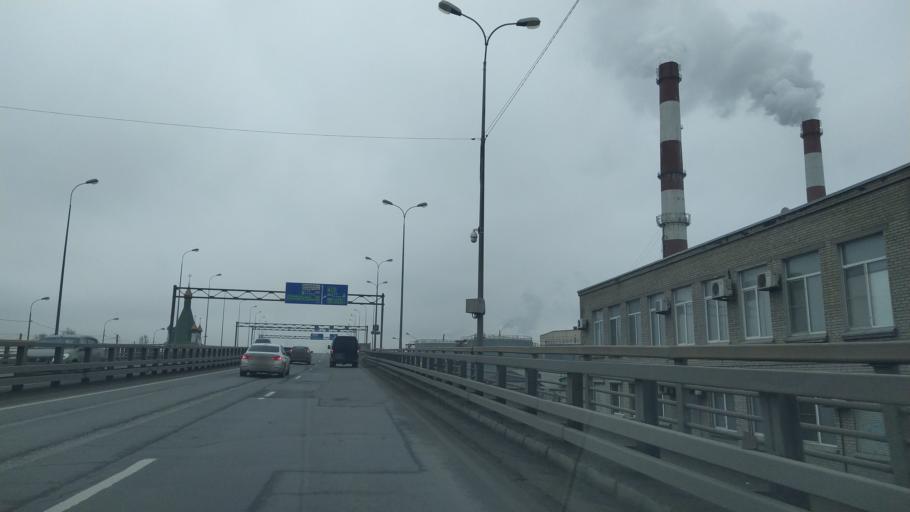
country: RU
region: St.-Petersburg
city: Dachnoye
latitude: 59.8324
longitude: 30.2982
